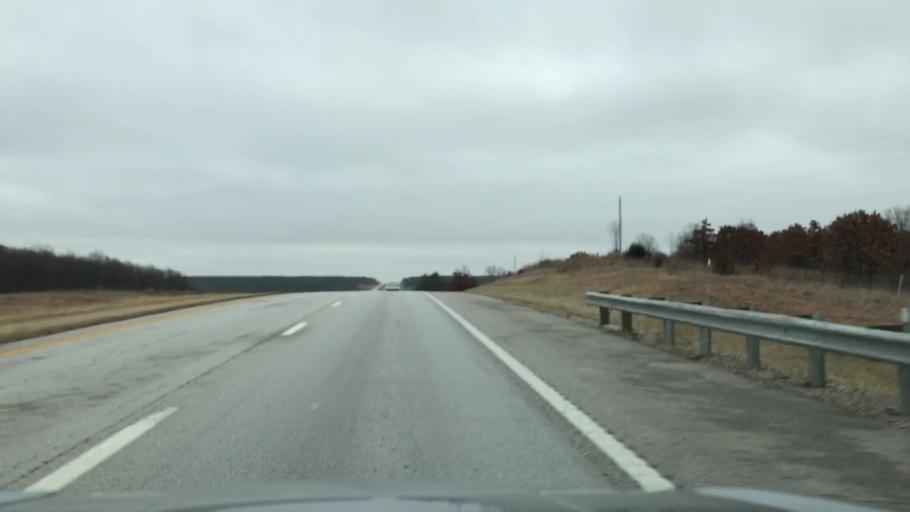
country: US
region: Missouri
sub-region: Linn County
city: Marceline
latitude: 39.7590
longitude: -92.8675
